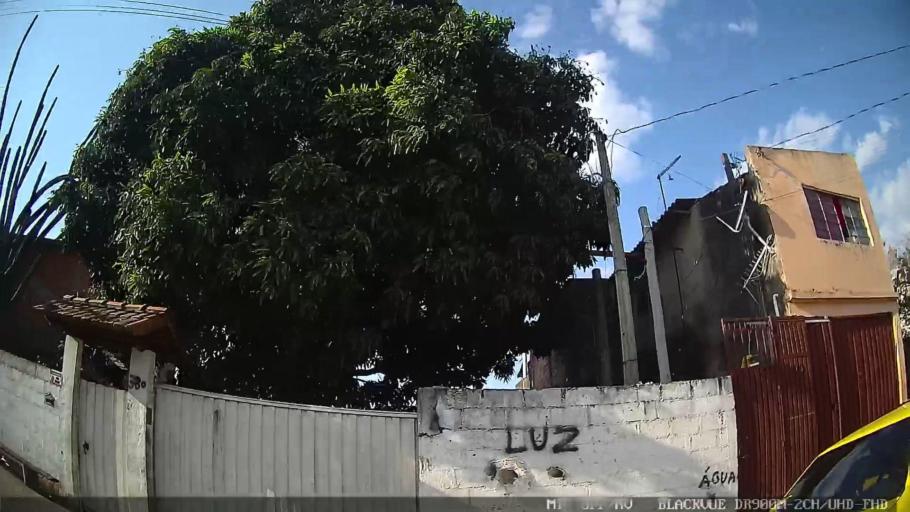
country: BR
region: Sao Paulo
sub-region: Cabreuva
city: Cabreuva
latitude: -23.2632
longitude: -47.0632
